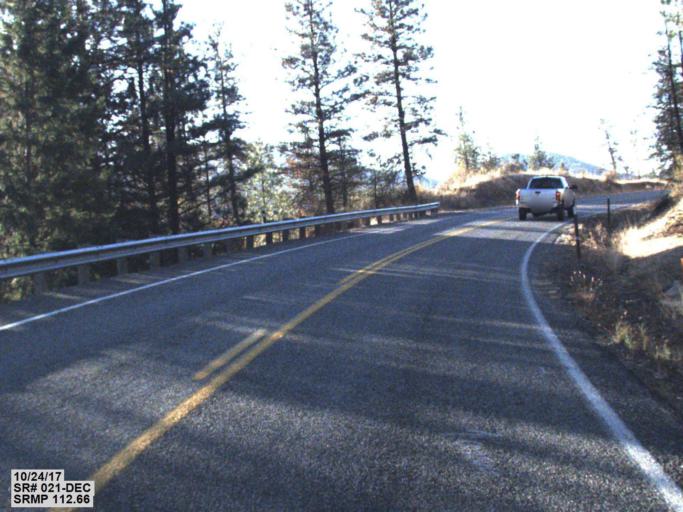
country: US
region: Washington
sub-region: Okanogan County
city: Coulee Dam
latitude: 48.0244
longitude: -118.6713
